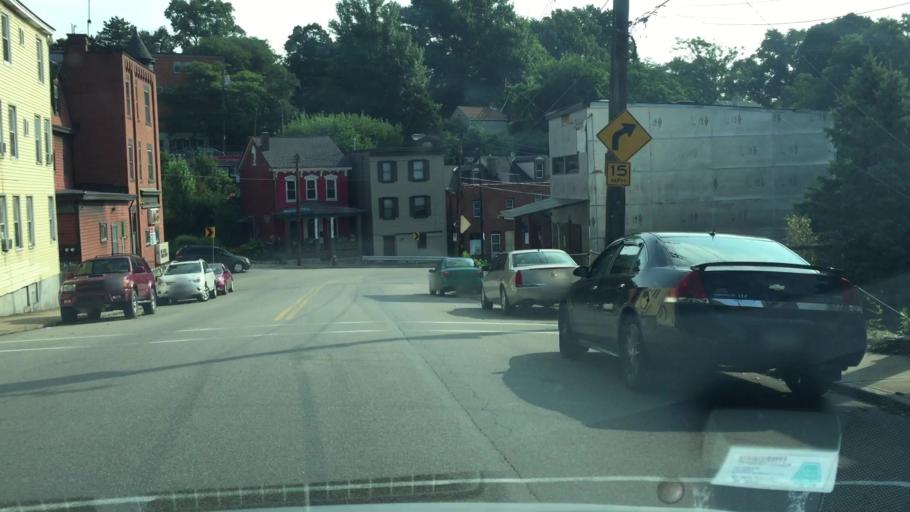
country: US
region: Pennsylvania
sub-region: Allegheny County
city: Mount Oliver
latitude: 40.4215
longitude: -79.9844
